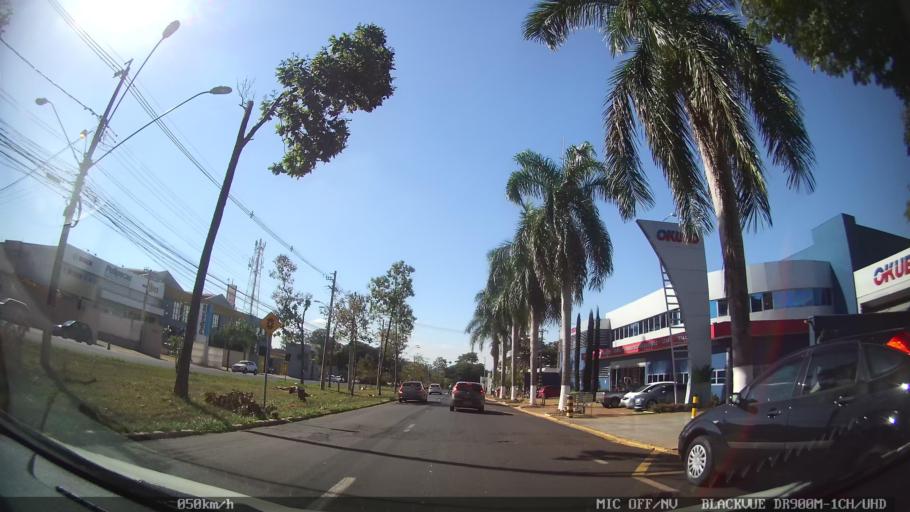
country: BR
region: Sao Paulo
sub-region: Ribeirao Preto
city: Ribeirao Preto
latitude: -21.1976
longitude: -47.7644
